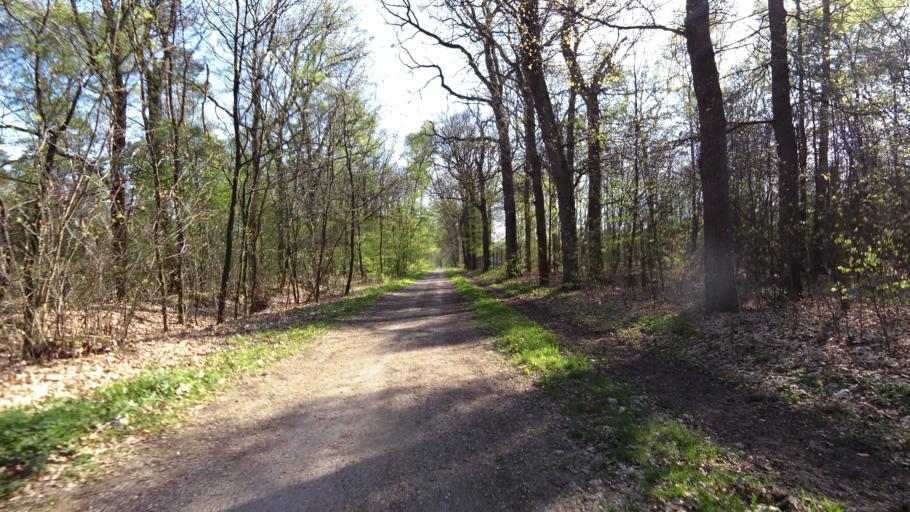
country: NL
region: Gelderland
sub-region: Gemeente Renkum
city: Oosterbeek
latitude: 52.0226
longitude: 5.8369
